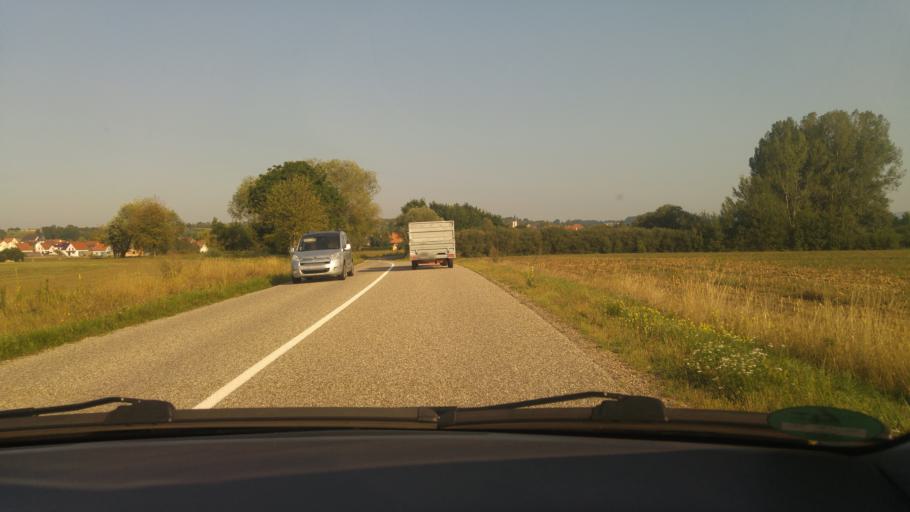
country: FR
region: Alsace
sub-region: Departement du Bas-Rhin
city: Eschbach
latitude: 48.8874
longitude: 7.7498
